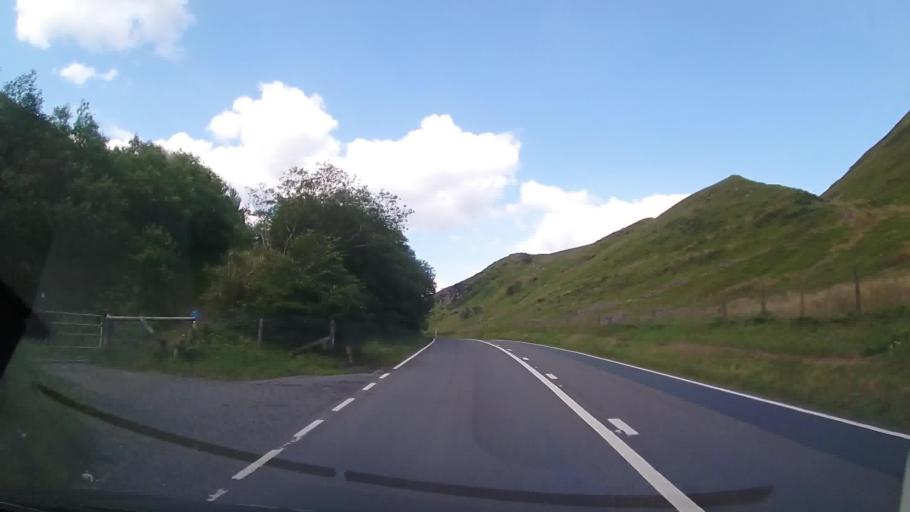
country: GB
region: Wales
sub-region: Gwynedd
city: Dolgellau
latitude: 52.7076
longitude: -3.8426
